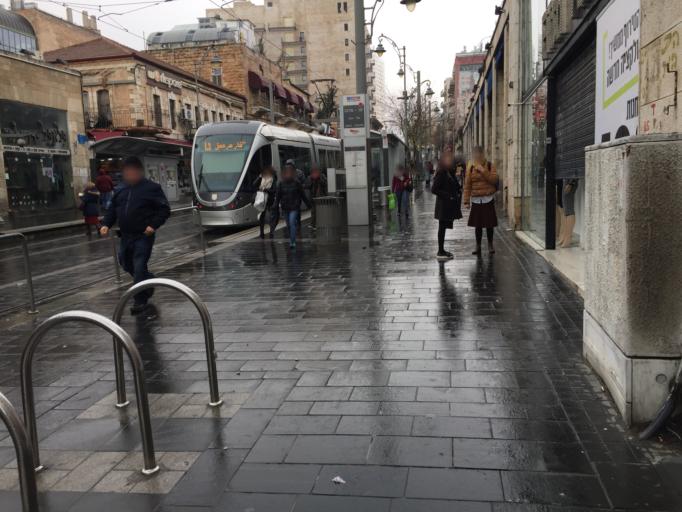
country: IL
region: Jerusalem
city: West Jerusalem
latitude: 31.7827
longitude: 35.2187
